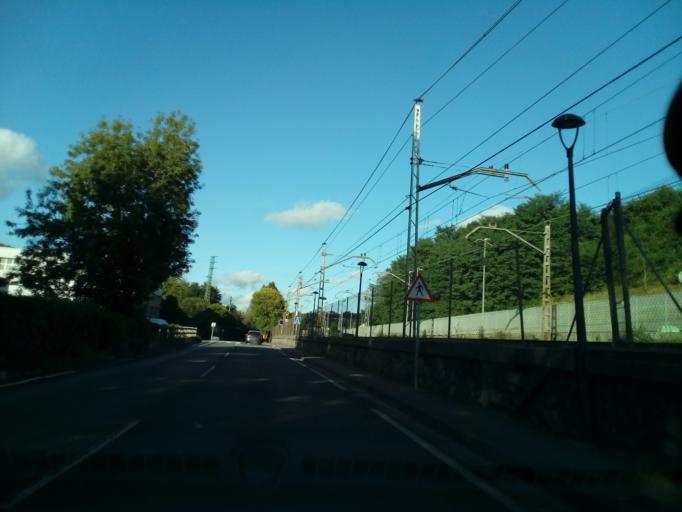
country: ES
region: Basque Country
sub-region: Provincia de Guipuzcoa
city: Andoain
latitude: 43.2243
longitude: -2.0121
